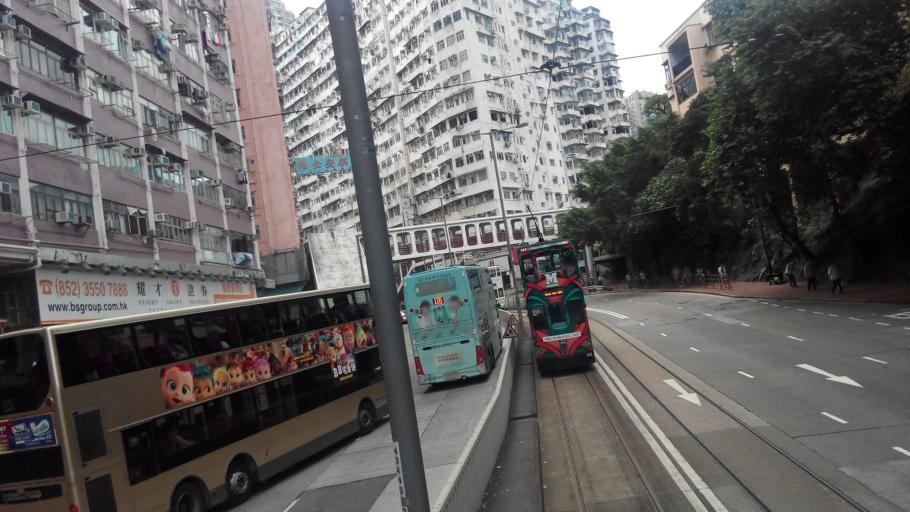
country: HK
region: Wanchai
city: Wan Chai
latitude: 22.2856
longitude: 114.2113
